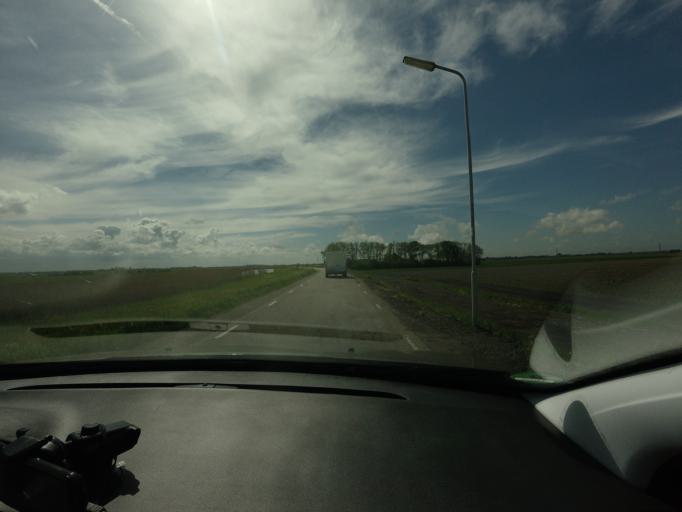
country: NL
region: North Holland
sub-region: Gemeente Heerhugowaard
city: Heerhugowaard
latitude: 52.5978
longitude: 4.8739
